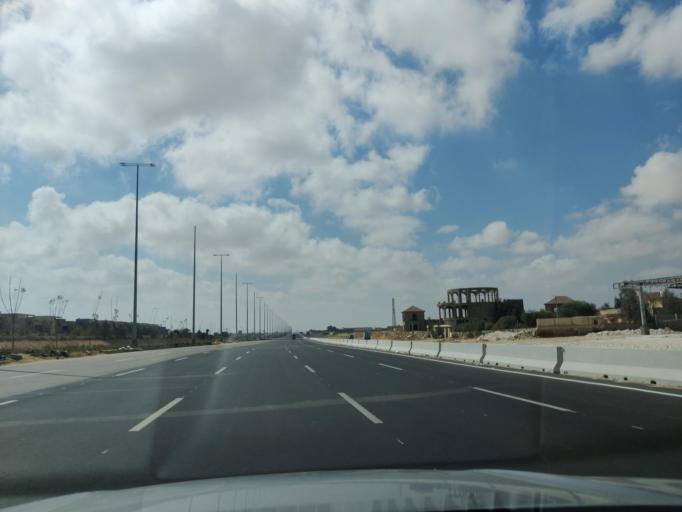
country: EG
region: Muhafazat Matruh
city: Al `Alamayn
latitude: 30.9397
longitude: 28.7836
